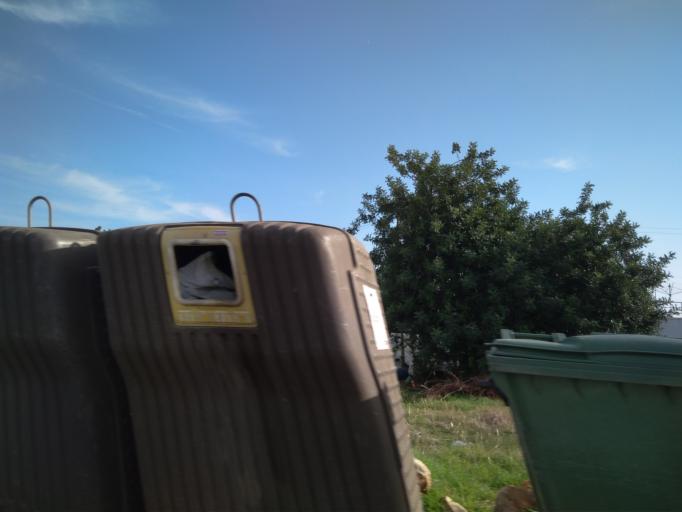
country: PT
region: Faro
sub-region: Faro
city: Santa Barbara de Nexe
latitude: 37.0913
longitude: -7.9185
